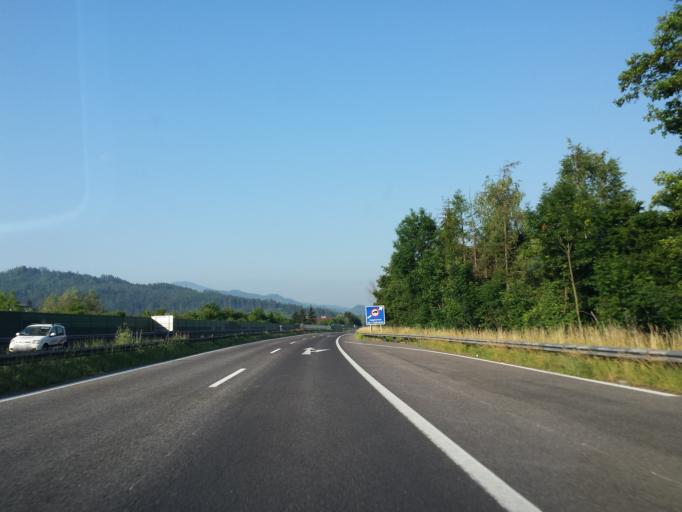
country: AT
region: Styria
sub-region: Politischer Bezirk Bruck-Muerzzuschlag
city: Kindberg
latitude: 47.4988
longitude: 15.4363
